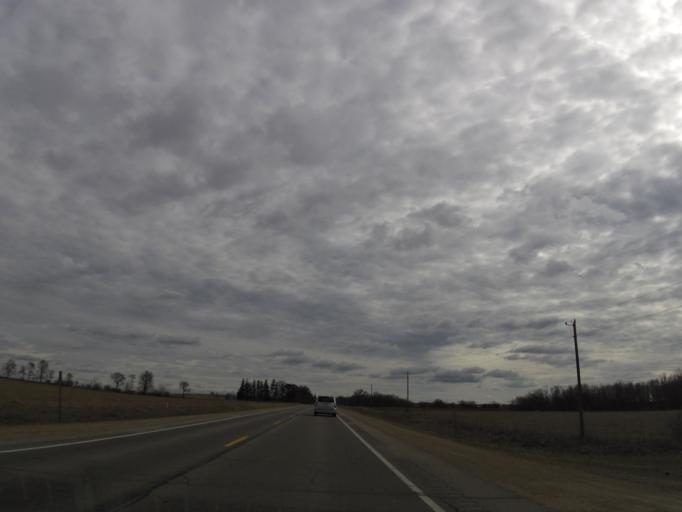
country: US
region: Iowa
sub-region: Chickasaw County
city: New Hampton
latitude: 43.2090
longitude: -92.2984
